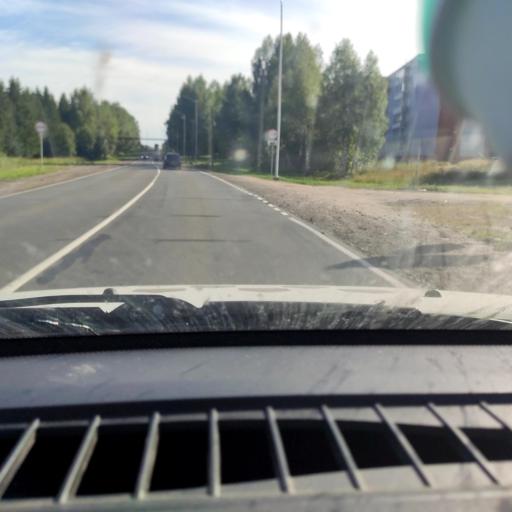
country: RU
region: Kirov
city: Vakhrushi
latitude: 58.6900
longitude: 50.0417
